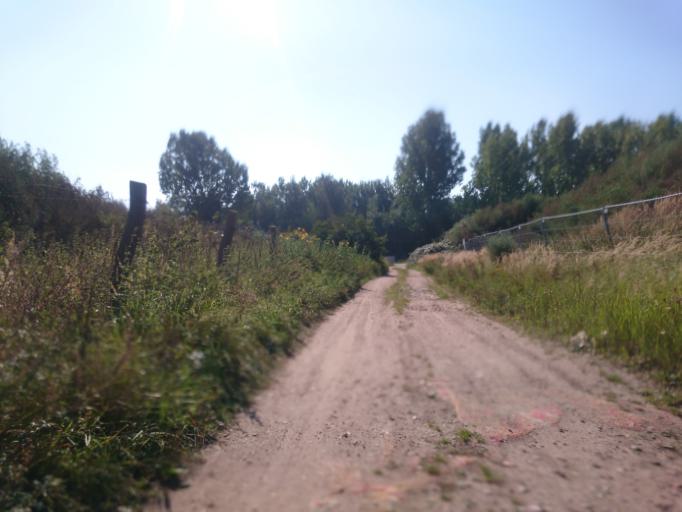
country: DE
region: Mecklenburg-Vorpommern
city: Barth
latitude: 54.3595
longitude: 12.6844
